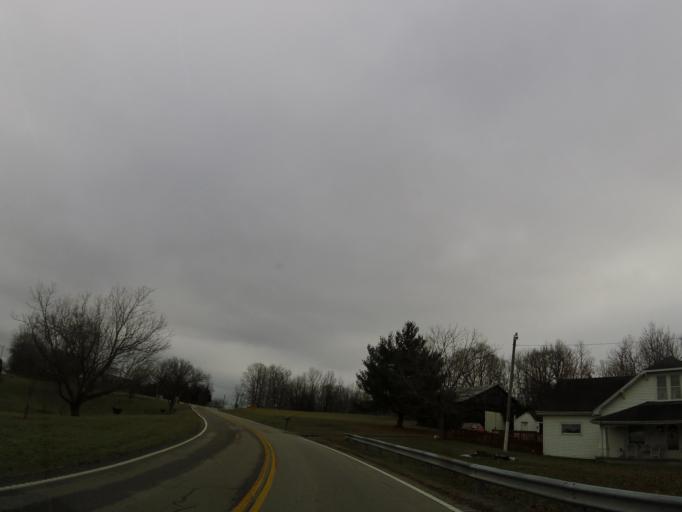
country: US
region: Kentucky
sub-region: Franklin County
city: Frankfort
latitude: 38.3398
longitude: -84.9630
